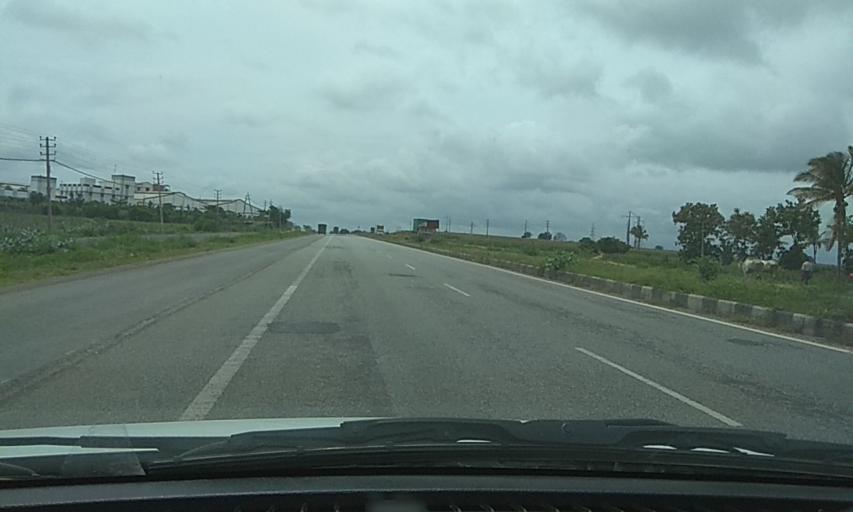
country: IN
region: Karnataka
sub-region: Davanagere
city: Mayakonda
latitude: 14.3381
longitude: 76.2112
